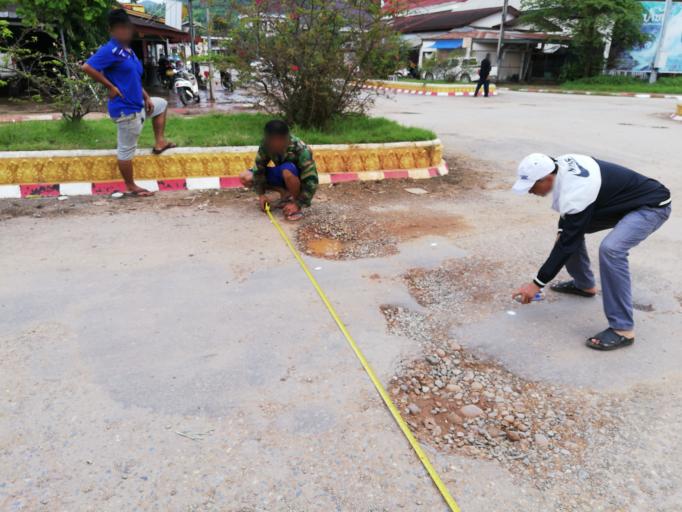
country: LA
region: Loungnamtha
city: Louang Namtha
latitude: 21.0029
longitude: 101.4075
